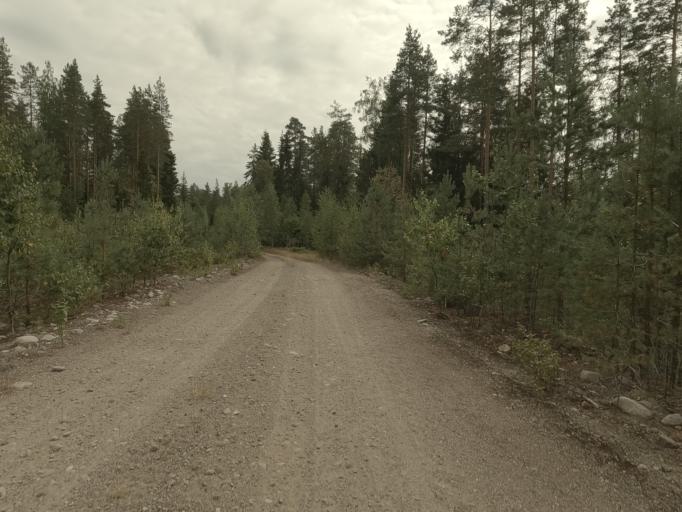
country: RU
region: Leningrad
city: Kamennogorsk
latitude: 61.0200
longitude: 29.1901
